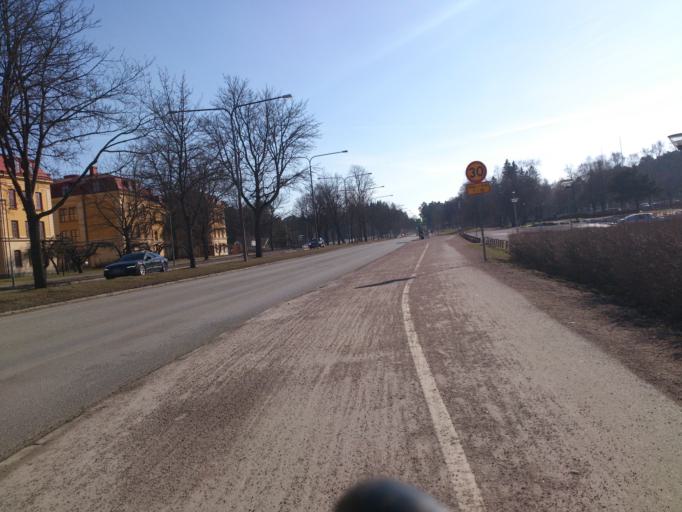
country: SE
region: Uppsala
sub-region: Uppsala Kommun
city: Uppsala
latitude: 59.8441
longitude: 17.6380
